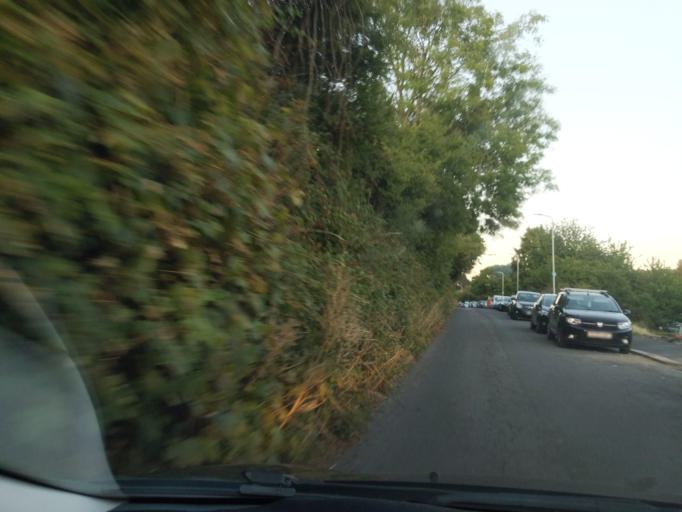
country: GB
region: England
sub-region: Cornwall
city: Torpoint
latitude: 50.4033
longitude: -4.1964
